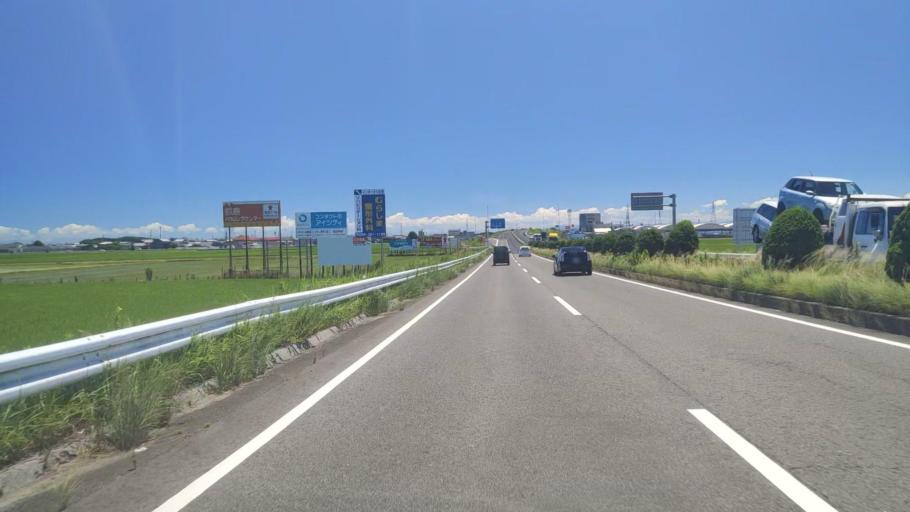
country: JP
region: Mie
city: Suzuka
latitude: 34.8797
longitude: 136.5964
